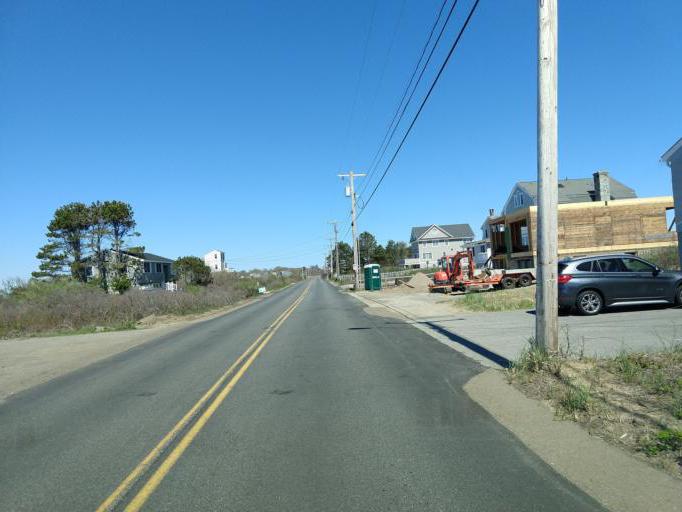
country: US
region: Maine
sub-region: York County
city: Old Orchard Beach
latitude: 43.4397
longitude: -70.3618
